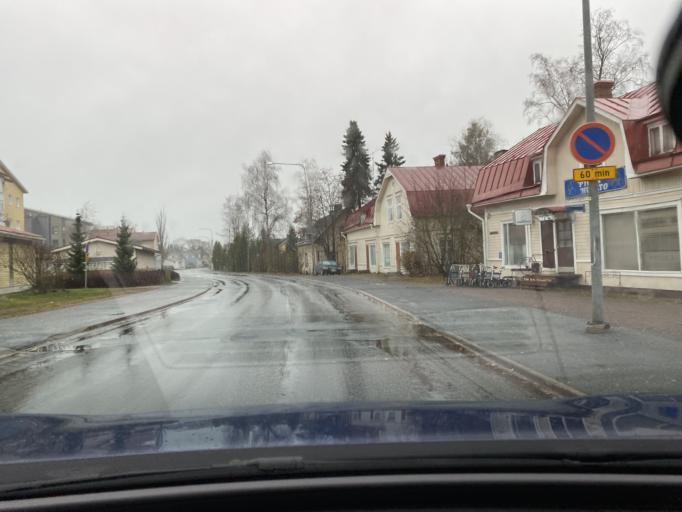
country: FI
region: Varsinais-Suomi
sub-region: Loimaa
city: Loimaa
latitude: 60.8535
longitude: 23.0561
